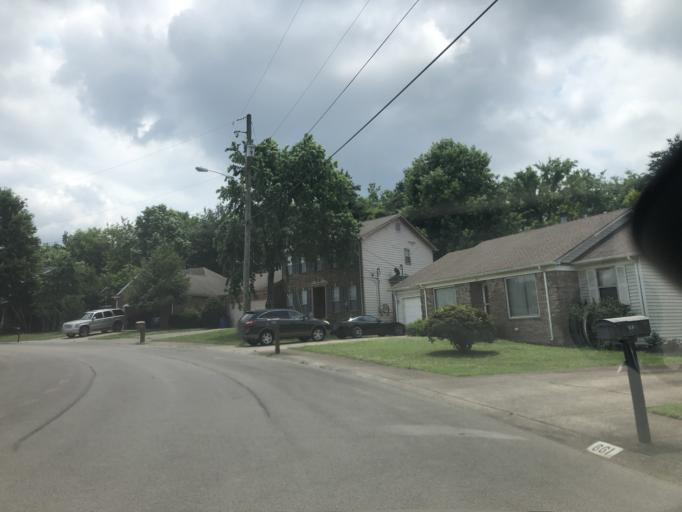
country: US
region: Tennessee
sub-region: Davidson County
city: Lakewood
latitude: 36.2191
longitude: -86.6290
